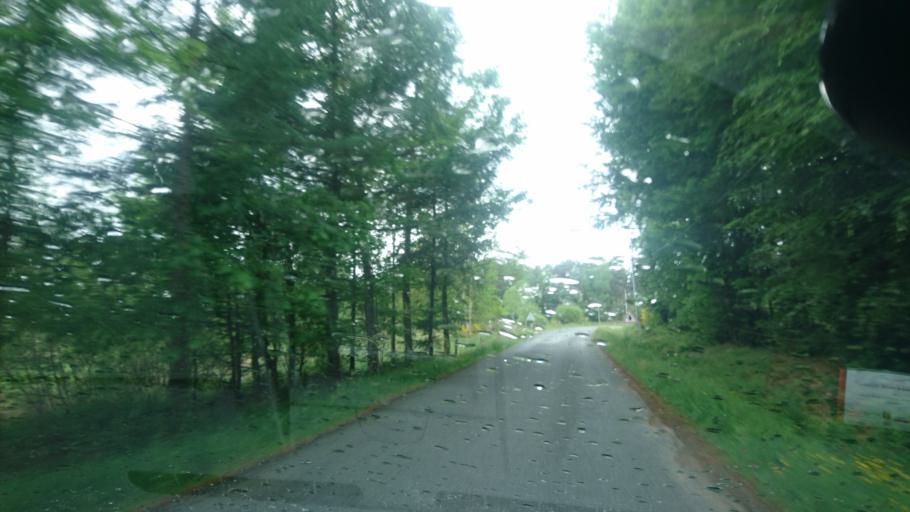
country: FR
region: Limousin
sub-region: Departement de la Haute-Vienne
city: Peyrat-le-Chateau
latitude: 45.8309
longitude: 1.8545
